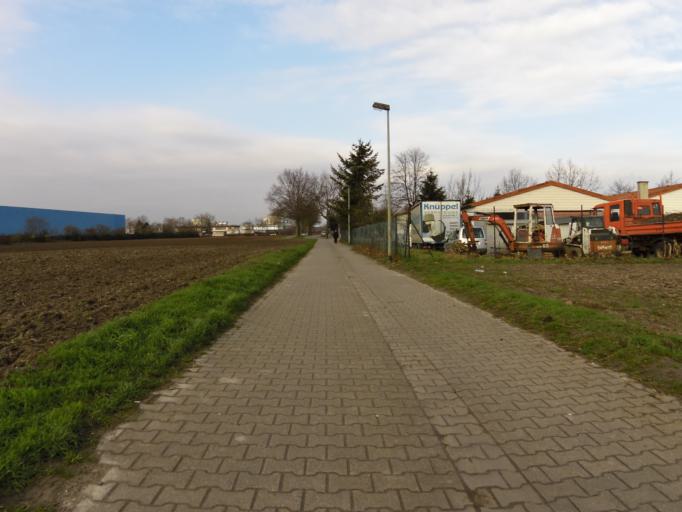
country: DE
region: Rheinland-Pfalz
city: Worms
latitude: 49.6113
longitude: 8.3503
